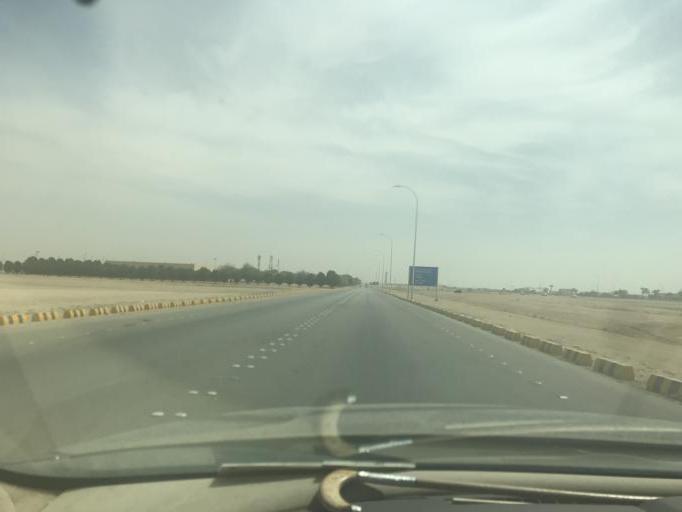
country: SA
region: Ar Riyad
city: Riyadh
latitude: 24.9870
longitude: 46.6889
